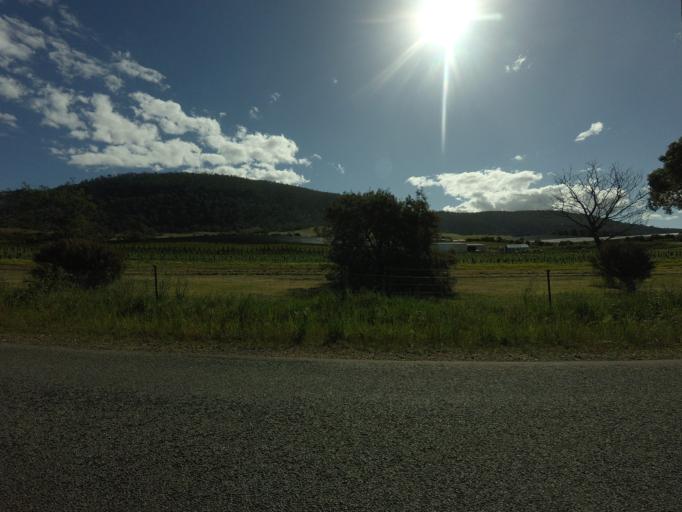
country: AU
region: Tasmania
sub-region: Sorell
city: Sorell
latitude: -42.6275
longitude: 147.4288
